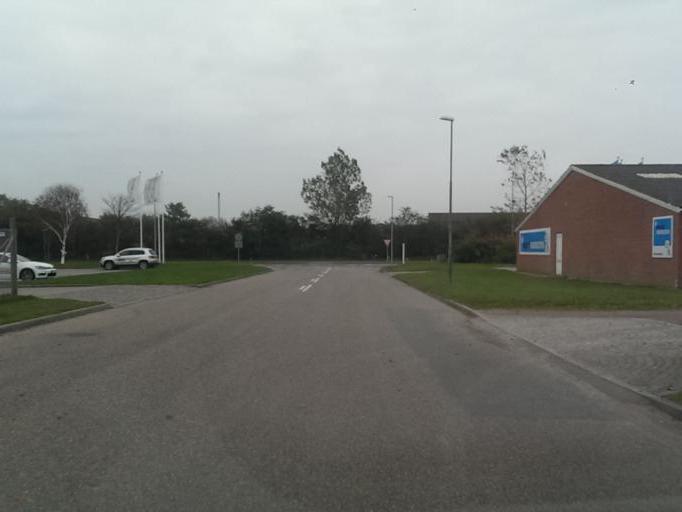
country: DK
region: South Denmark
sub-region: Esbjerg Kommune
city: Esbjerg
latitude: 55.5048
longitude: 8.4669
